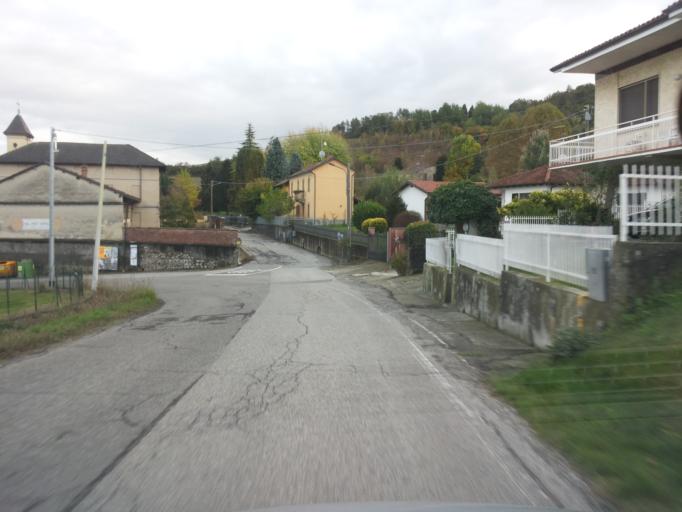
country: IT
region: Piedmont
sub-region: Provincia di Alessandria
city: Serralunga di Crea
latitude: 45.0993
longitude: 8.2928
